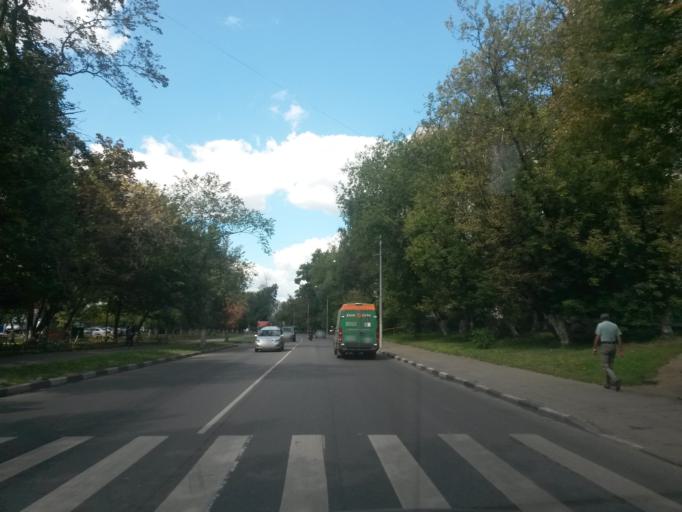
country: RU
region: Moscow
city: Tekstil'shchiki
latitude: 55.6828
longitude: 37.7243
